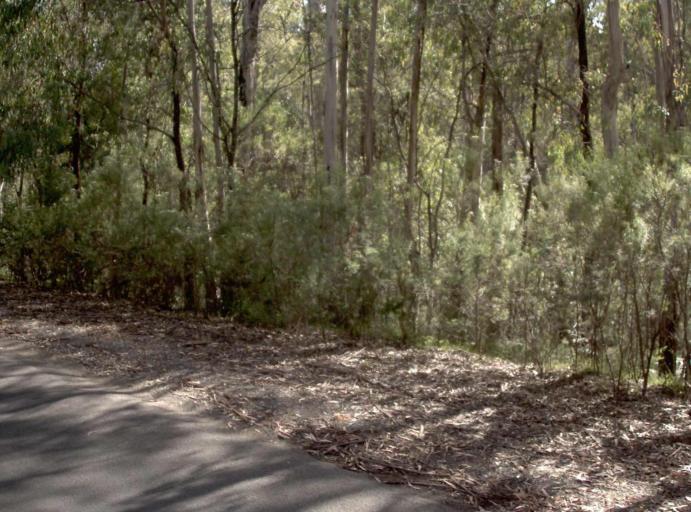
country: AU
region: Victoria
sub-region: East Gippsland
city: Lakes Entrance
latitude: -37.4572
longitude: 148.1219
